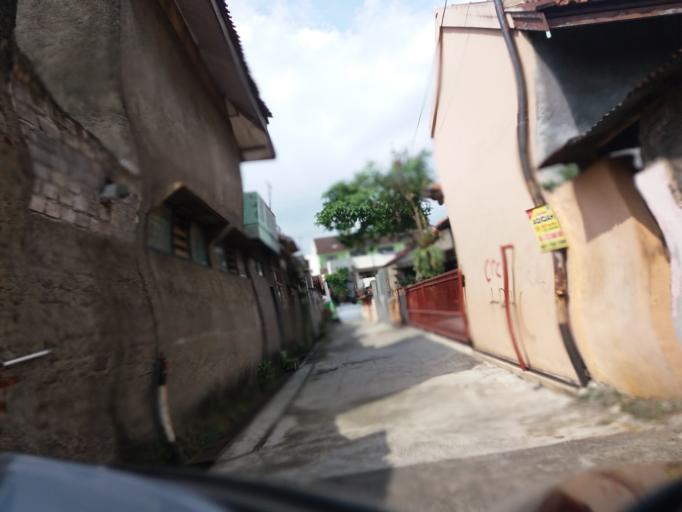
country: ID
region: West Java
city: Bandung
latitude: -6.9247
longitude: 107.6544
